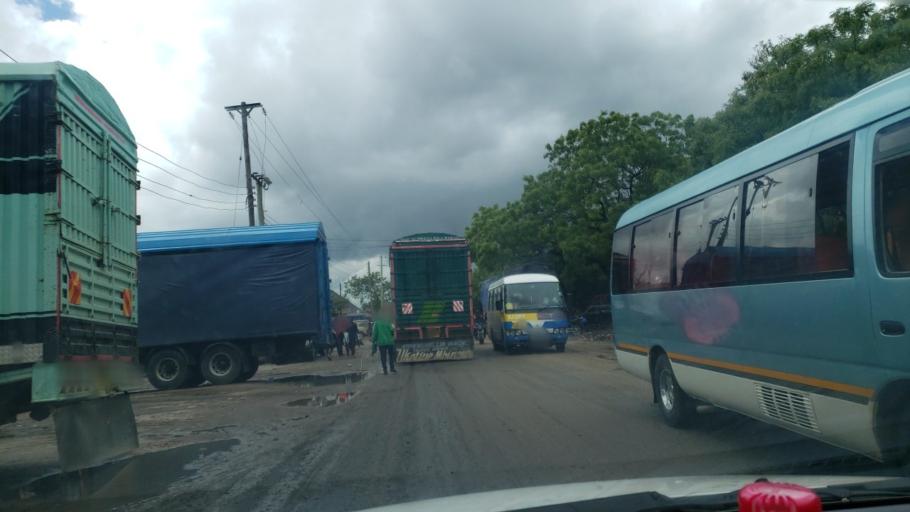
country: TZ
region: Dar es Salaam
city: Magomeni
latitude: -6.8029
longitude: 39.2246
